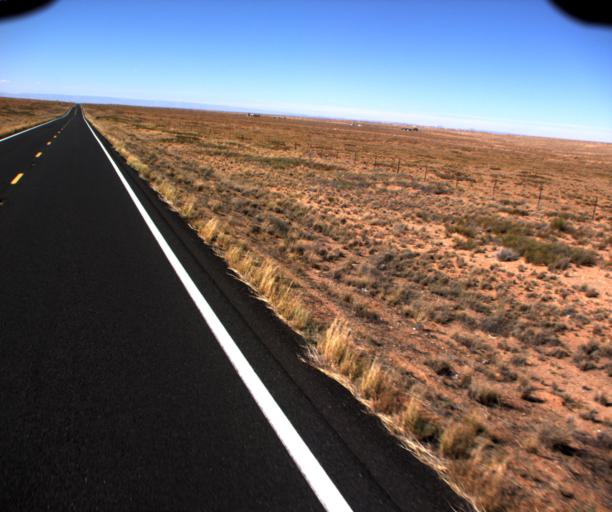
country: US
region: Arizona
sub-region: Coconino County
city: Tuba City
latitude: 36.0164
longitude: -111.0990
